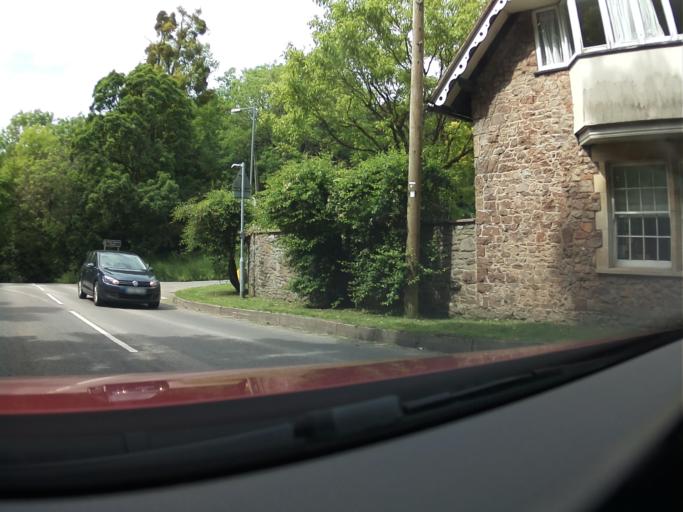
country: GB
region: England
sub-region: North Somerset
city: Easton-in-Gordano
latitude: 51.4946
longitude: -2.6596
